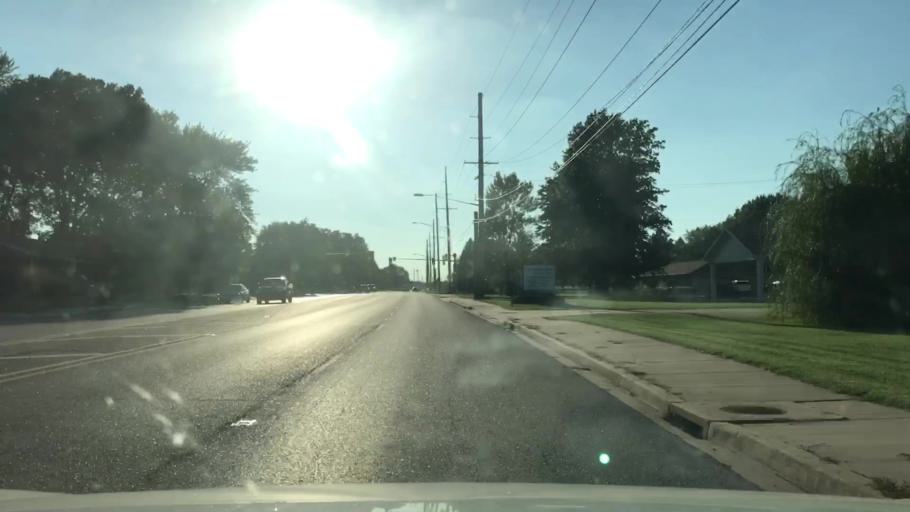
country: US
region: Illinois
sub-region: Madison County
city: Granite City
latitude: 38.7316
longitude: -90.1294
